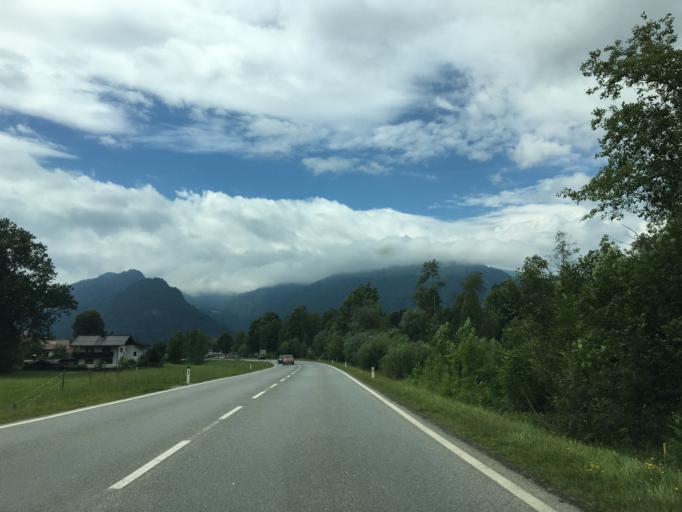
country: AT
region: Tyrol
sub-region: Politischer Bezirk Kitzbuhel
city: Kossen
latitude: 47.6614
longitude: 12.4206
